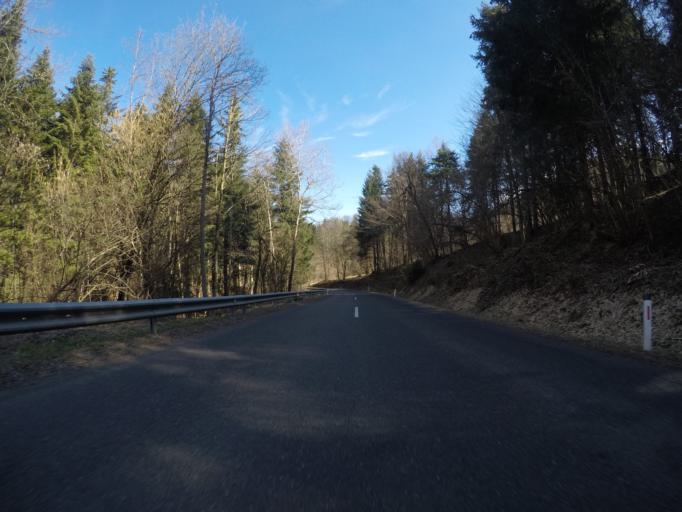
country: SI
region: Lovrenc na Pohorju
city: Lovrenc na Pohorju
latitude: 46.5433
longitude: 15.4430
